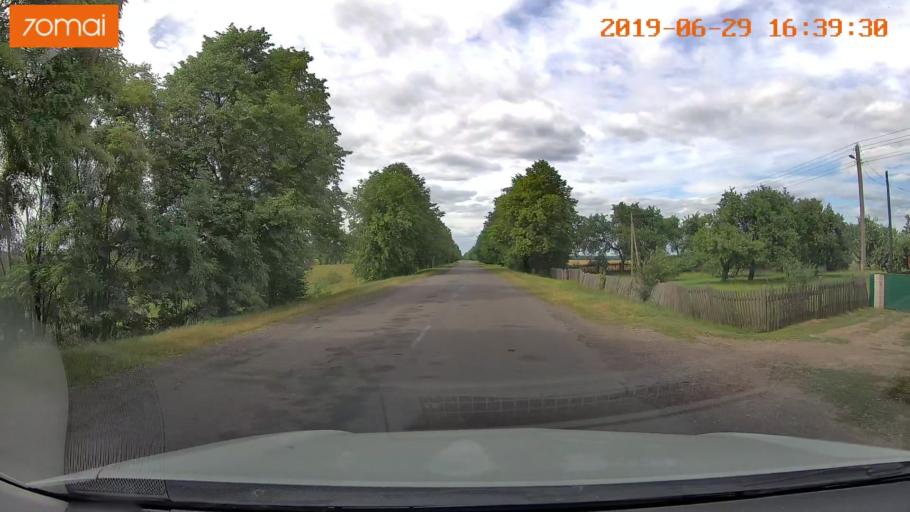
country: BY
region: Brest
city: Luninyets
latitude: 52.2432
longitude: 27.0163
